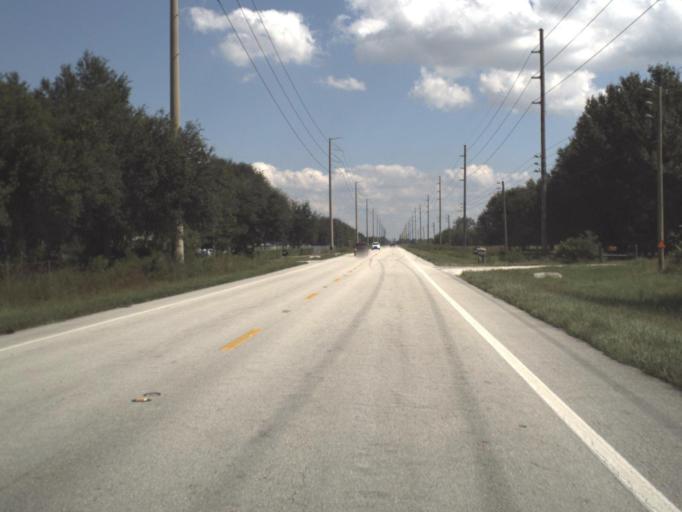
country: US
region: Florida
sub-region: Highlands County
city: Sebring
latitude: 27.4124
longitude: -81.5029
